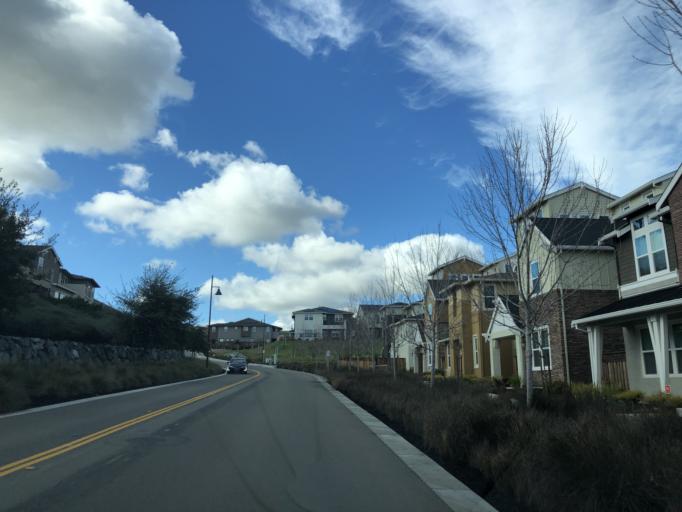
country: US
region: California
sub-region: Alameda County
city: Dublin
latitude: 37.7361
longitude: -121.8768
